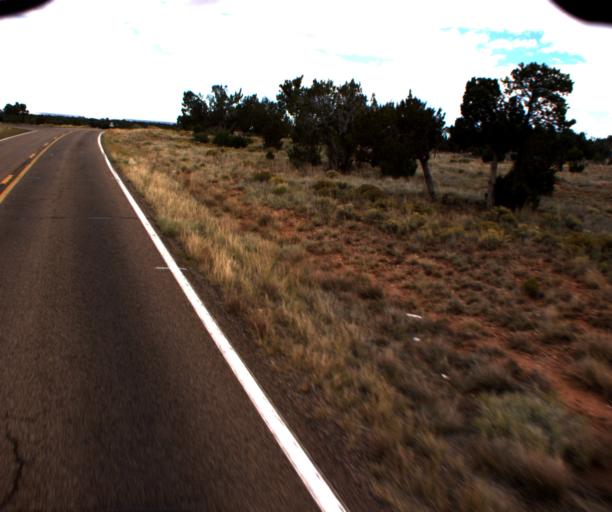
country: US
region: Arizona
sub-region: Navajo County
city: Heber-Overgaard
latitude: 34.5034
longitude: -110.4515
